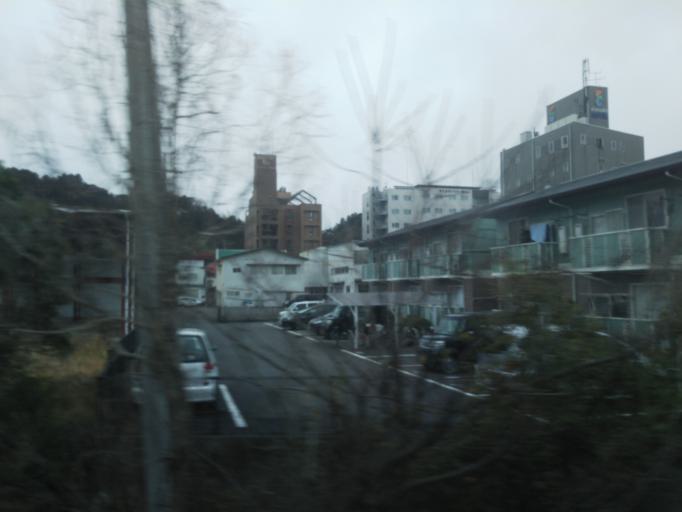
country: JP
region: Kochi
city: Nakamura
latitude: 32.9818
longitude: 132.9463
